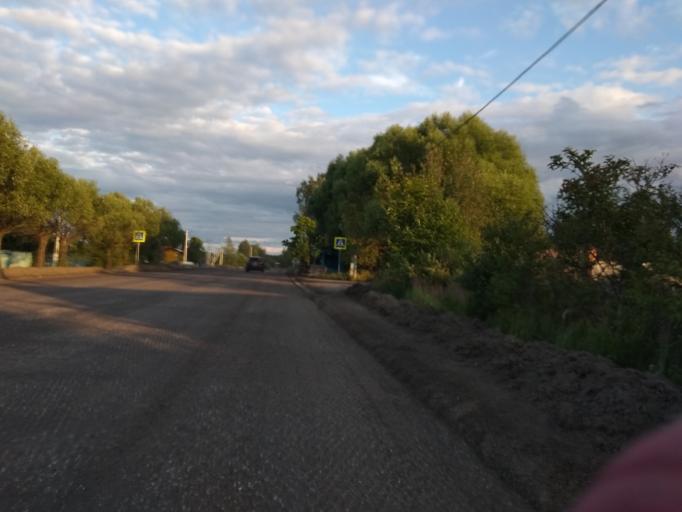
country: RU
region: Moskovskaya
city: Misheronskiy
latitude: 55.6500
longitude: 39.7557
